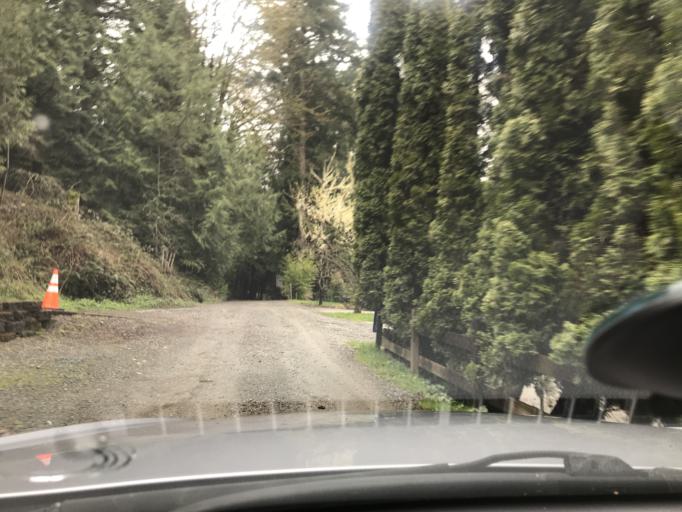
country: US
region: Washington
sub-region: King County
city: Ames Lake
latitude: 47.6403
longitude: -121.9523
